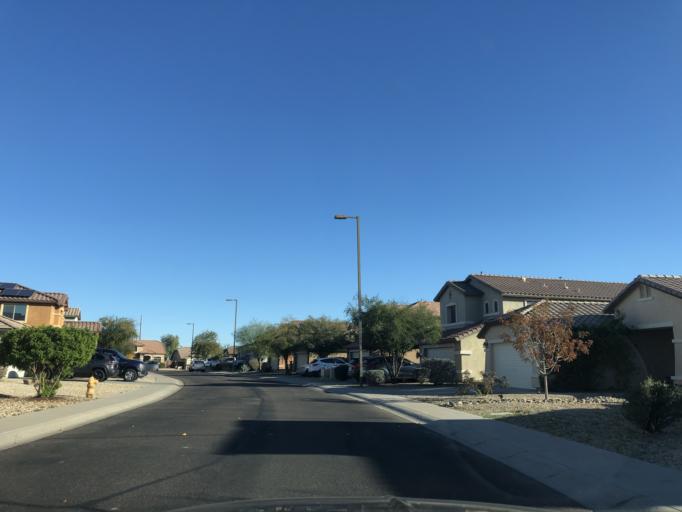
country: US
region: Arizona
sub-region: Maricopa County
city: Buckeye
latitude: 33.4253
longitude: -112.6058
